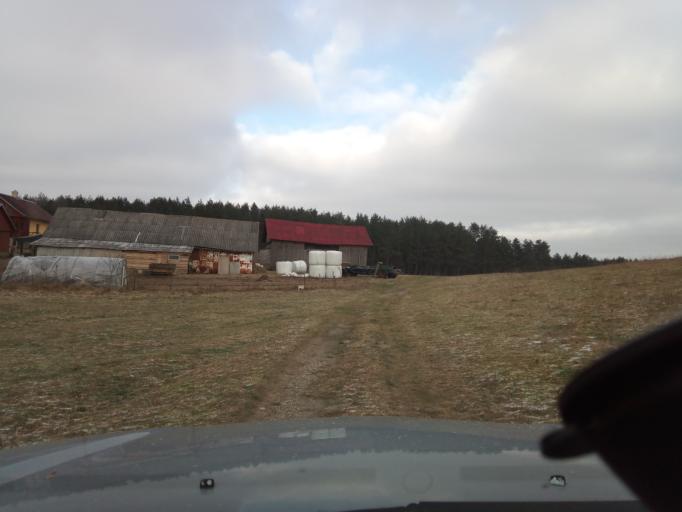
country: LT
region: Alytaus apskritis
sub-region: Alytaus rajonas
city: Daugai
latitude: 54.3320
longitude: 24.2860
